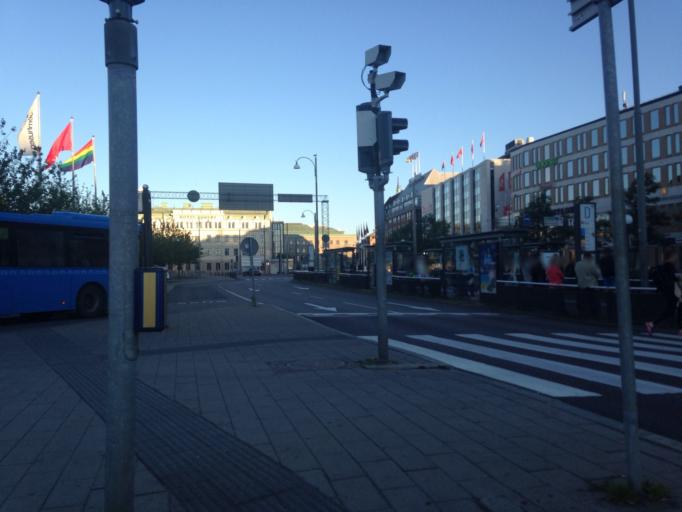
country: SE
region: Vaestra Goetaland
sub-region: Goteborg
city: Goeteborg
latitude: 57.7096
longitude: 11.9711
